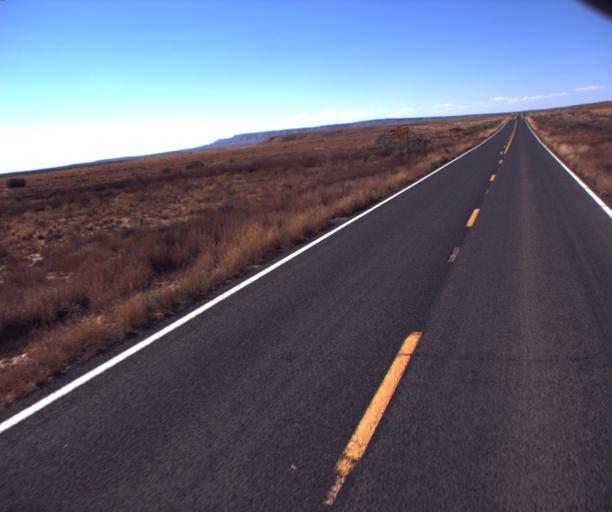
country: US
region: Arizona
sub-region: Navajo County
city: First Mesa
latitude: 35.9793
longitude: -110.7396
